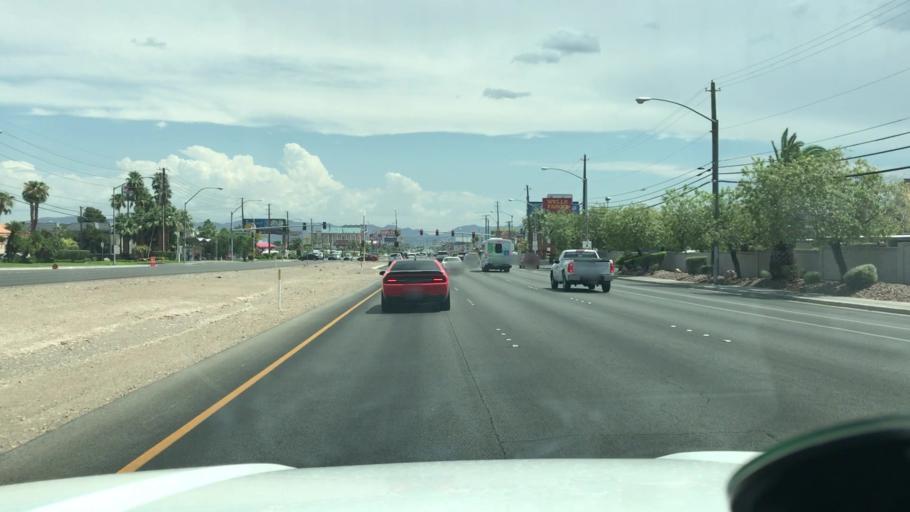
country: US
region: Nevada
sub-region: Clark County
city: Winchester
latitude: 36.1227
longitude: -115.0756
